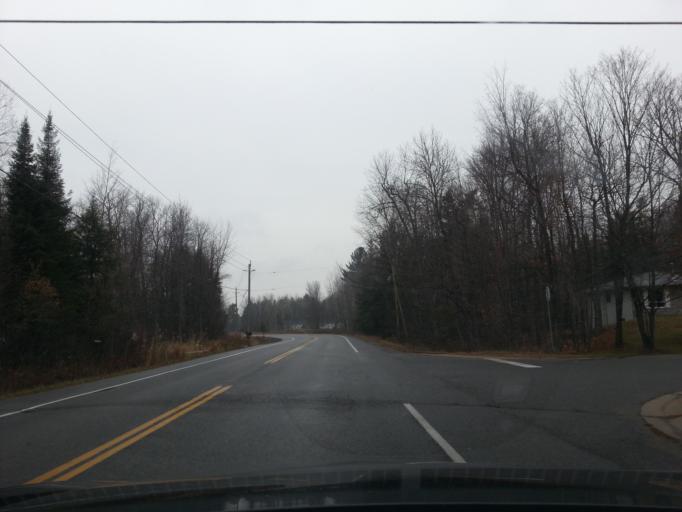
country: CA
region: Ontario
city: Carleton Place
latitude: 45.1392
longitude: -76.0764
